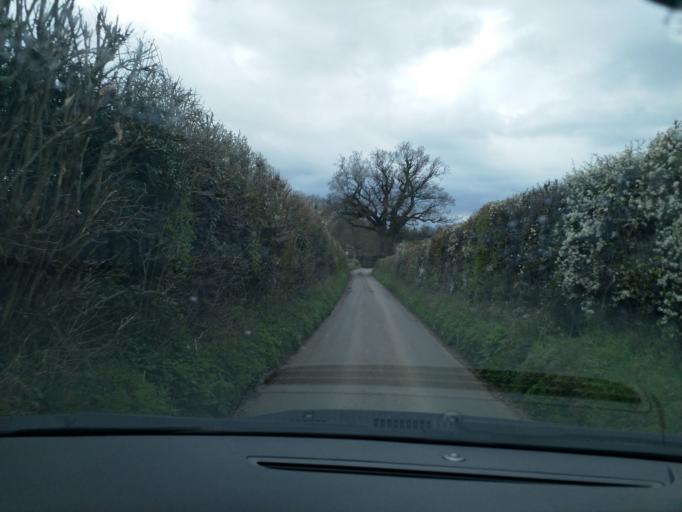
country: GB
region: England
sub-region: Warwickshire
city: Henley in Arden
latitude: 52.2905
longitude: -1.7457
